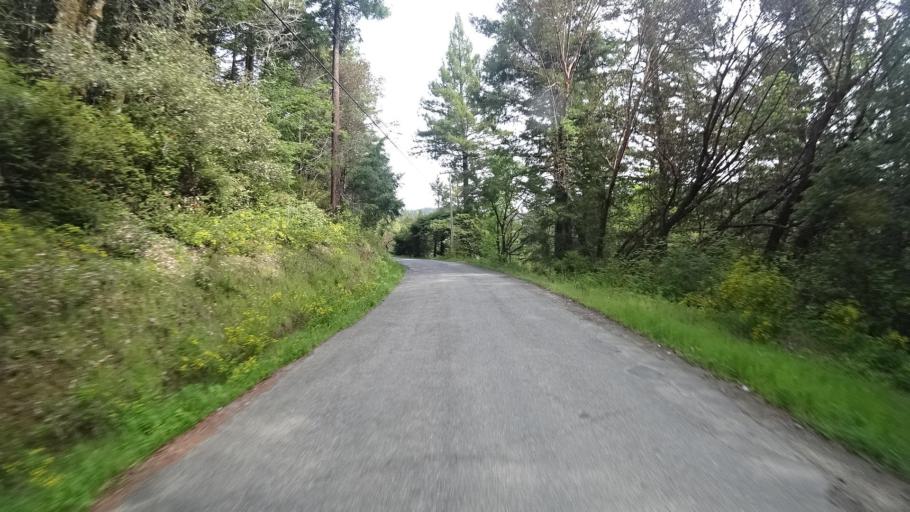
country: US
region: California
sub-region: Humboldt County
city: Redway
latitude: 40.2488
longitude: -123.8325
